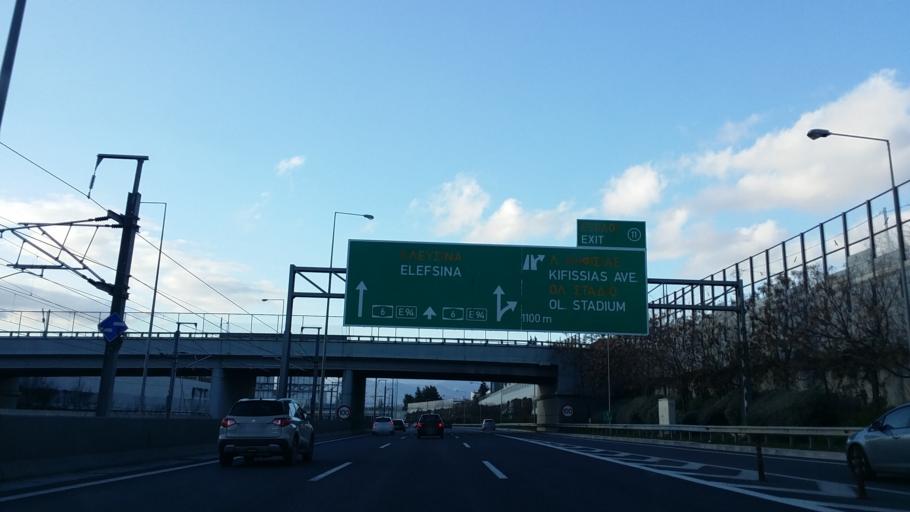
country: GR
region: Attica
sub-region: Nomarchia Athinas
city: Vrilissia
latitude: 38.0351
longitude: 23.8202
